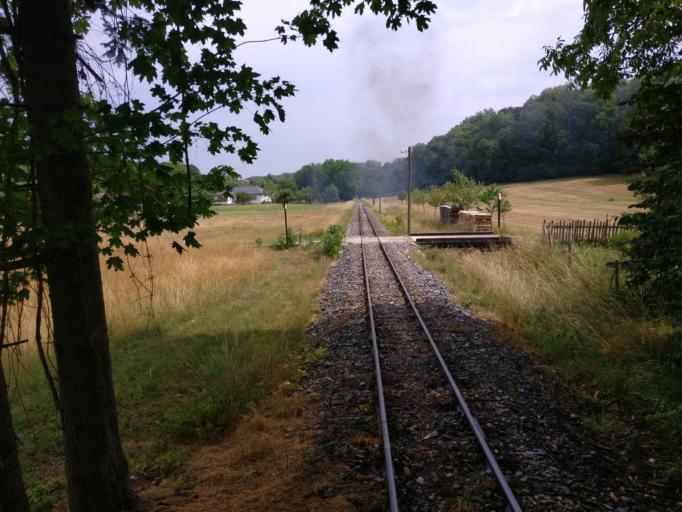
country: AT
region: Upper Austria
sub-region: Politischer Bezirk Steyr-Land
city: Sierning
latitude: 48.0220
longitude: 14.3295
